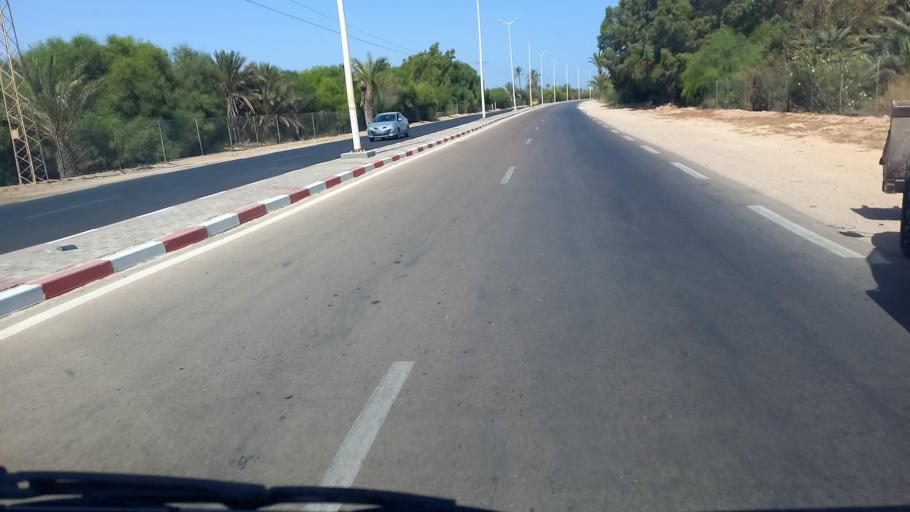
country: TN
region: Madanin
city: Midoun
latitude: 33.8284
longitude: 11.0106
